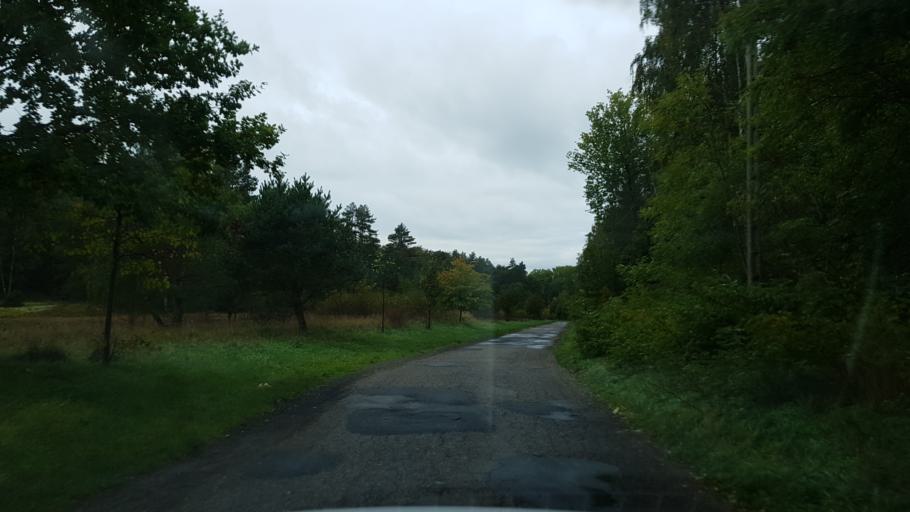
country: PL
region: West Pomeranian Voivodeship
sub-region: Powiat kamienski
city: Wolin
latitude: 53.8319
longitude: 14.6038
